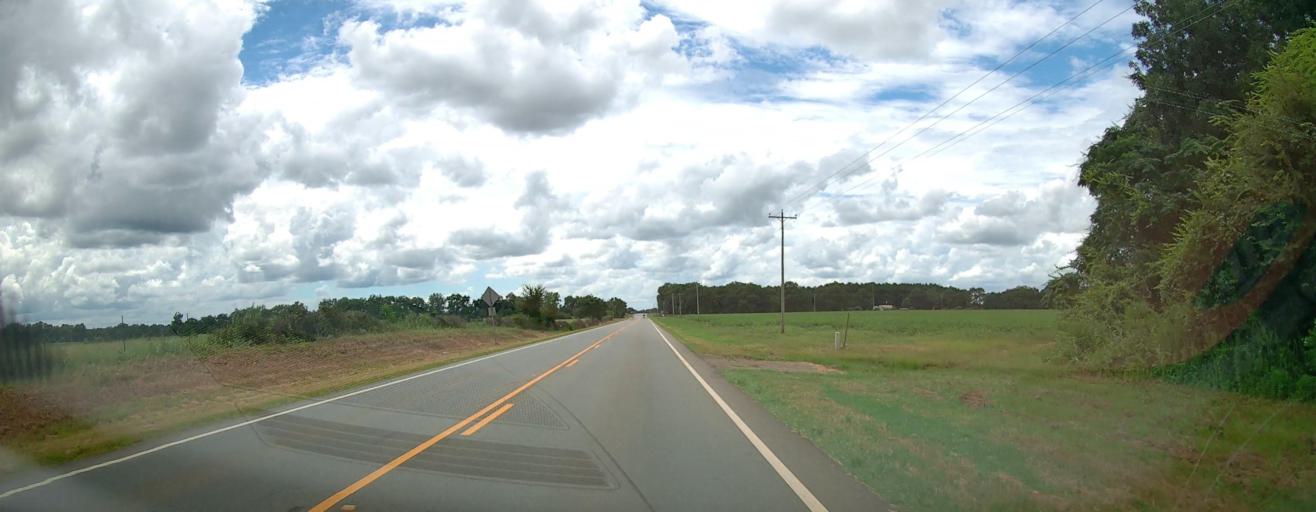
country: US
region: Georgia
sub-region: Macon County
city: Montezuma
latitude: 32.2914
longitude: -83.9203
